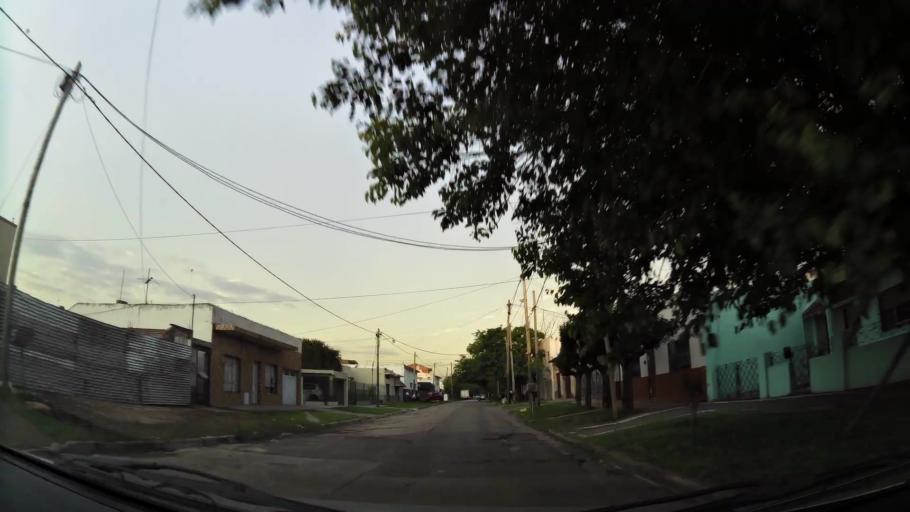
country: AR
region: Buenos Aires
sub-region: Partido de Lomas de Zamora
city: Lomas de Zamora
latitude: -34.7673
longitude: -58.3772
